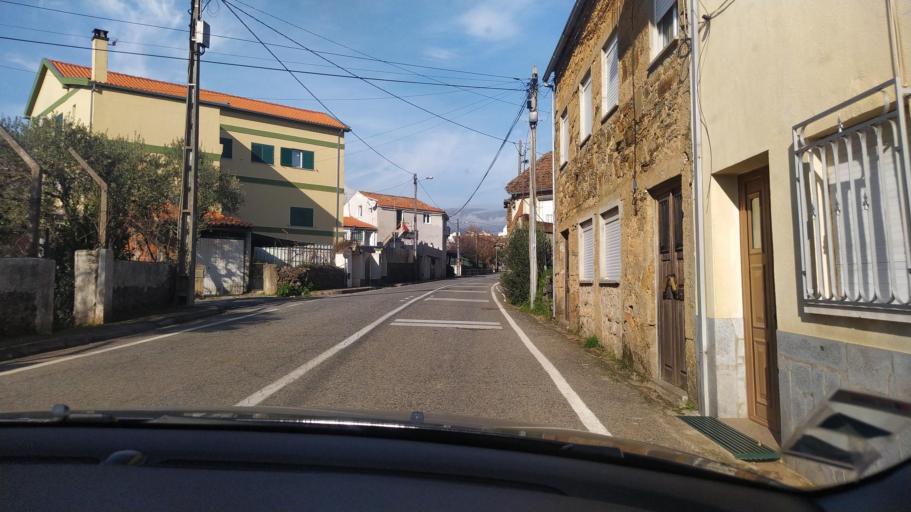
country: PT
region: Castelo Branco
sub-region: Concelho do Fundao
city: Aldeia de Joanes
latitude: 40.1969
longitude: -7.6392
